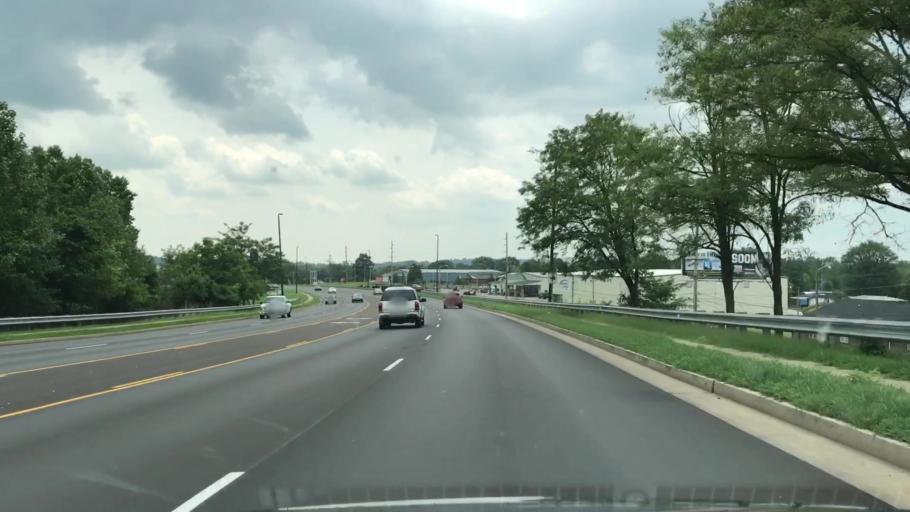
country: US
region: Kentucky
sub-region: Barren County
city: Glasgow
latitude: 36.9940
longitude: -85.9319
